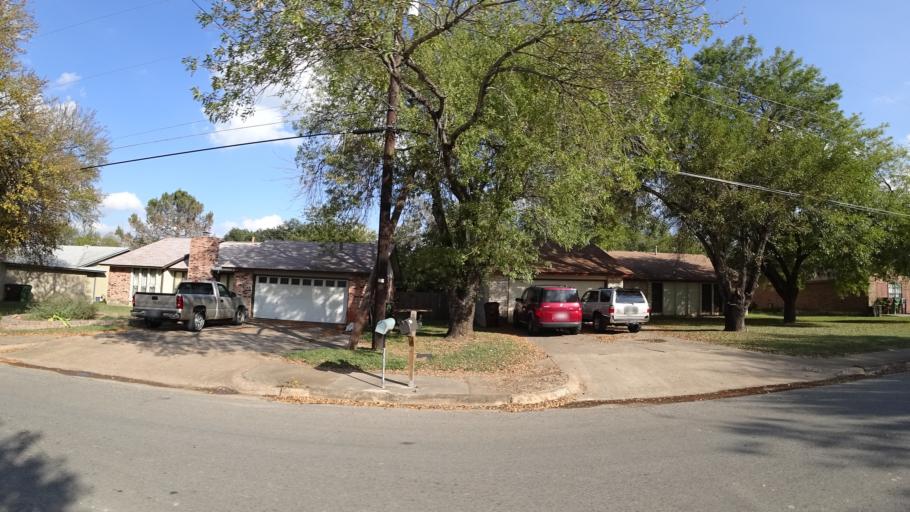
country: US
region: Texas
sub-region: Williamson County
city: Round Rock
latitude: 30.4948
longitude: -97.6749
